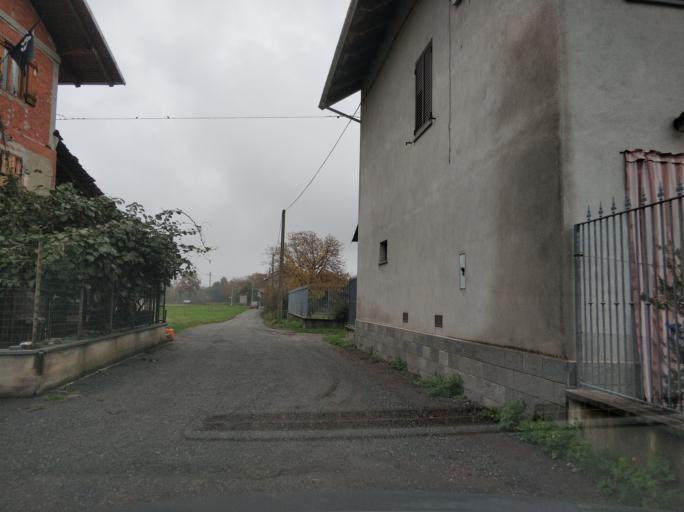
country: IT
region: Piedmont
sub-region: Provincia di Torino
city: Robassomero
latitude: 45.2188
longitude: 7.5723
